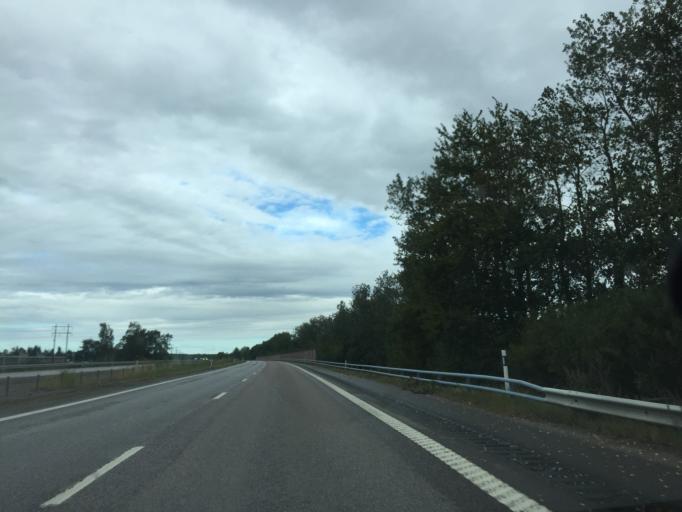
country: SE
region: Soedermanland
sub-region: Eskilstuna Kommun
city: Eskilstuna
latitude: 59.3884
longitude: 16.5136
